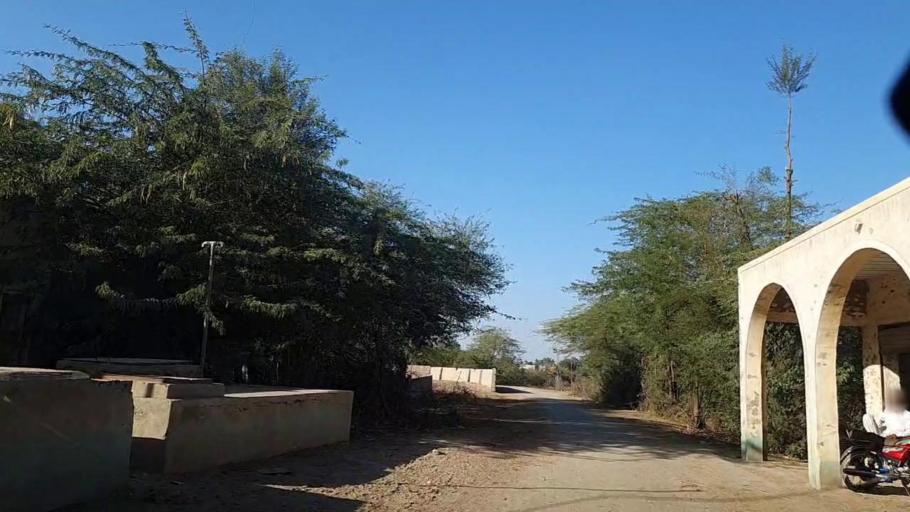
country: PK
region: Sindh
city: Khanpur
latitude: 27.7659
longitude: 69.2945
